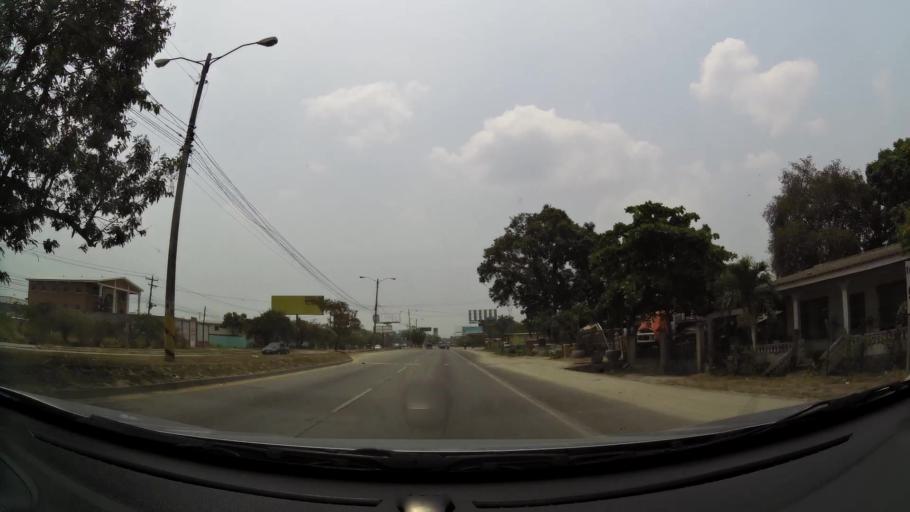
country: HN
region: Cortes
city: La Lima
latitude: 15.4568
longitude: -87.9522
